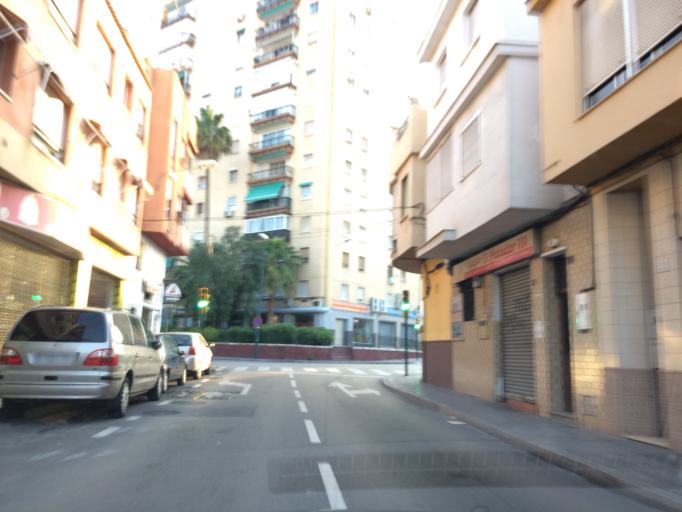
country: ES
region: Andalusia
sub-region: Provincia de Malaga
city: Malaga
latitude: 36.7345
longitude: -4.4228
